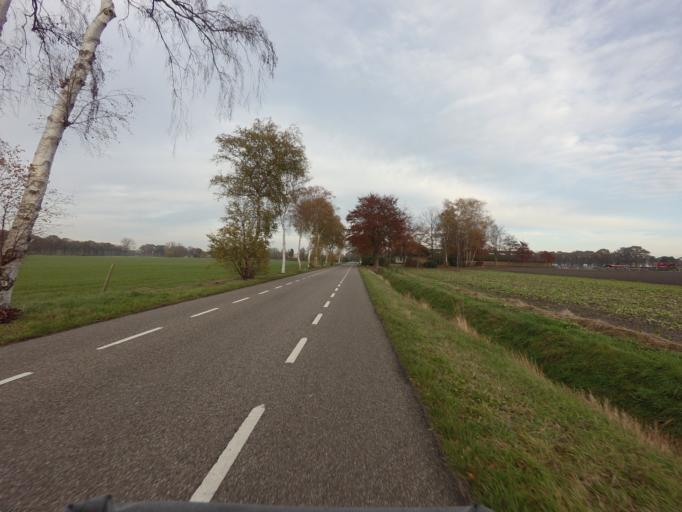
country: BE
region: Flanders
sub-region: Provincie Antwerpen
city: Hoogstraten
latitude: 51.4852
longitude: 4.8228
